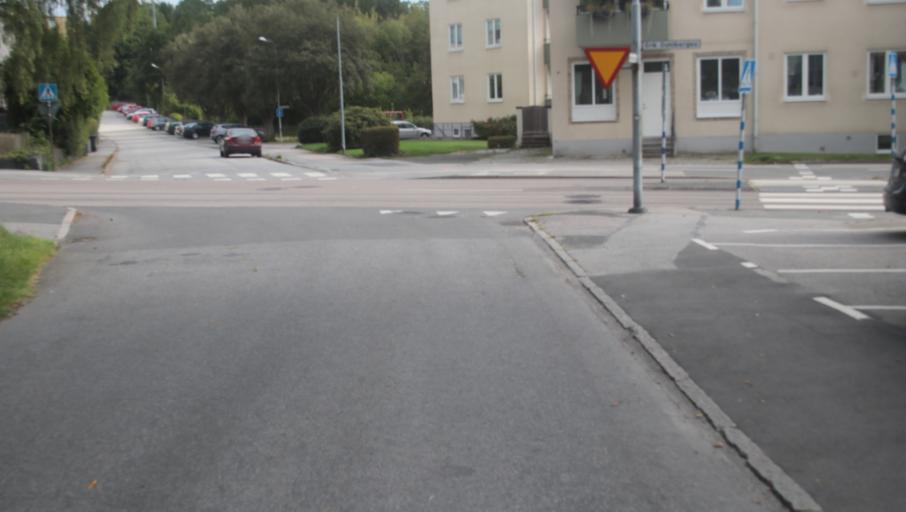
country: SE
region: Blekinge
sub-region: Karlshamns Kommun
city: Karlshamn
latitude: 56.1758
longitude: 14.8627
